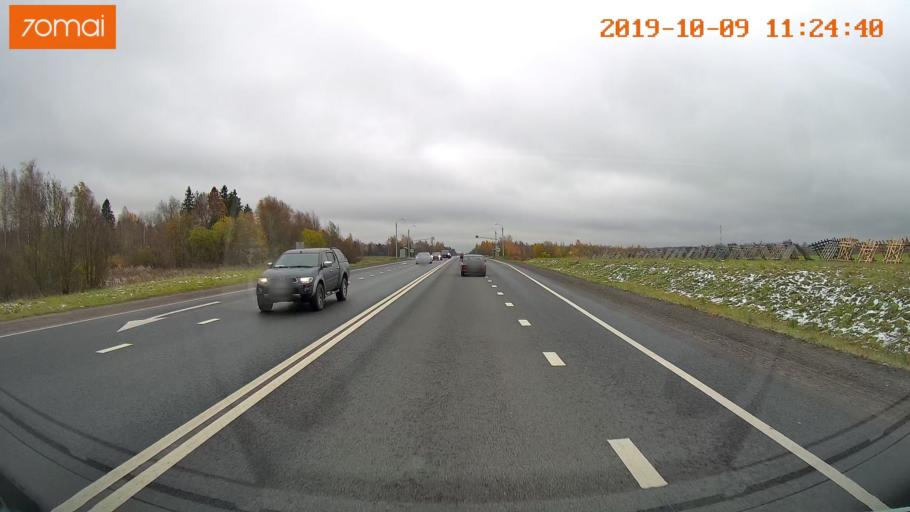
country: RU
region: Vologda
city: Vologda
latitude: 59.1093
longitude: 39.9823
